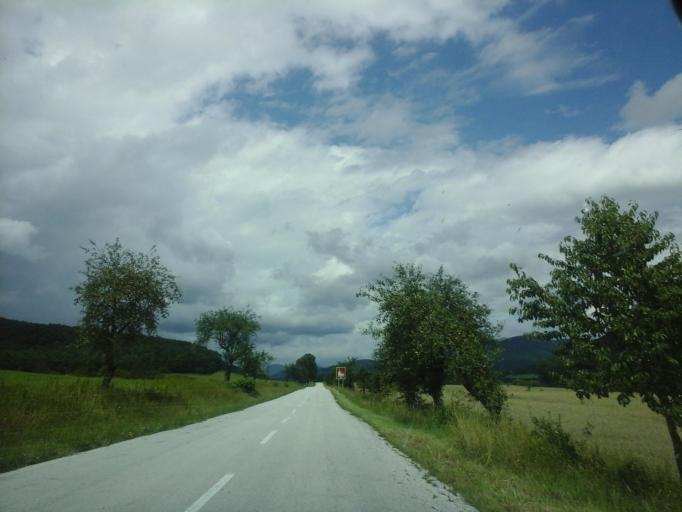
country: SK
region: Kosicky
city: Roznava
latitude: 48.6159
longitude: 20.3811
